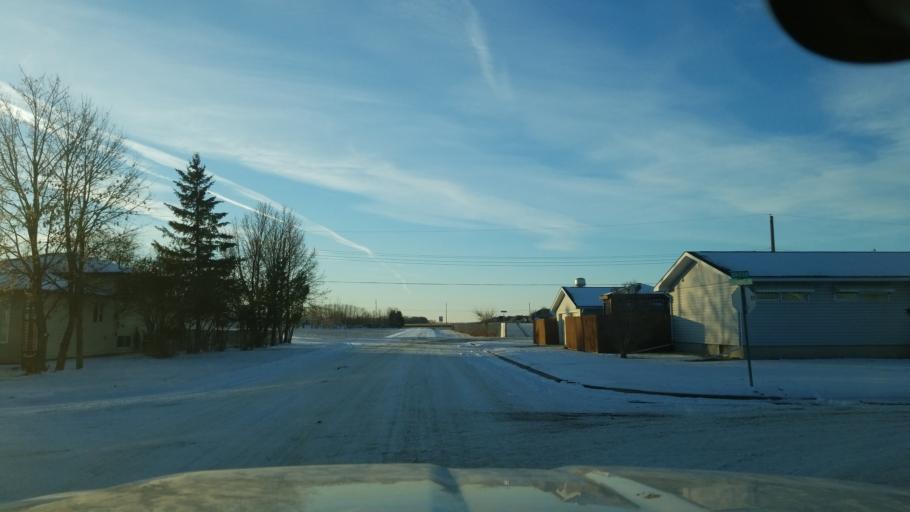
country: CA
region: Manitoba
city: Portage la Prairie
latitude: 49.9797
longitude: -98.3031
